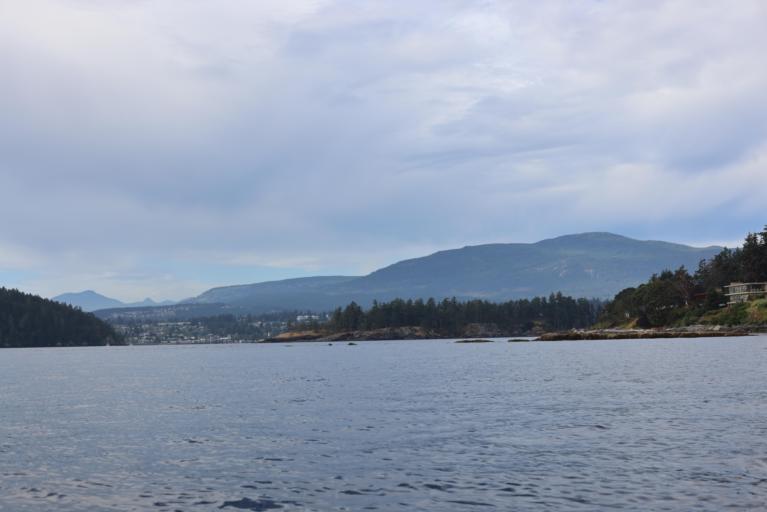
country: CA
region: British Columbia
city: Nanaimo
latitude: 49.2146
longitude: -123.9366
